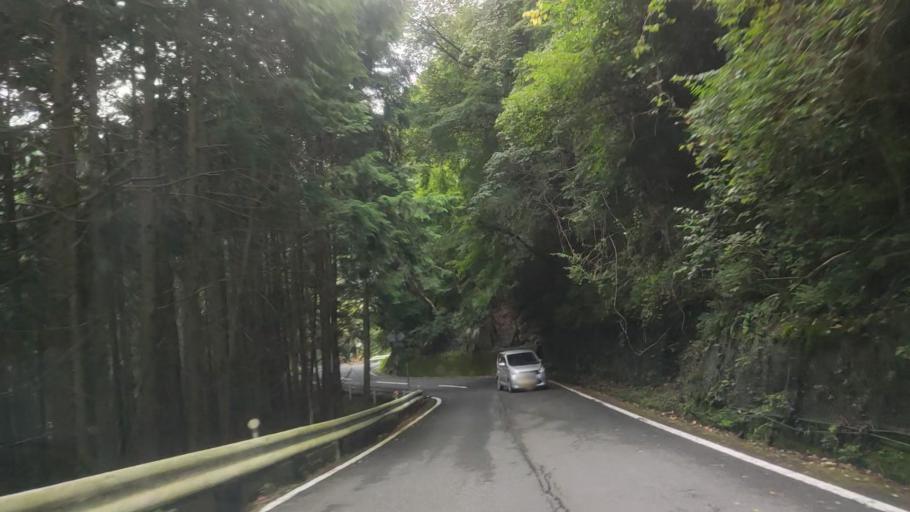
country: JP
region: Wakayama
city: Koya
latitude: 34.2414
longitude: 135.5477
